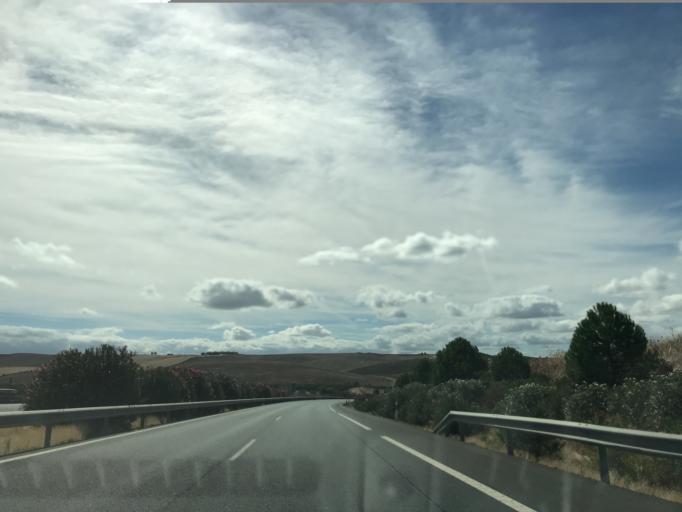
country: ES
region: Andalusia
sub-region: Province of Cordoba
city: La Victoria
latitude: 37.7395
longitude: -4.8501
